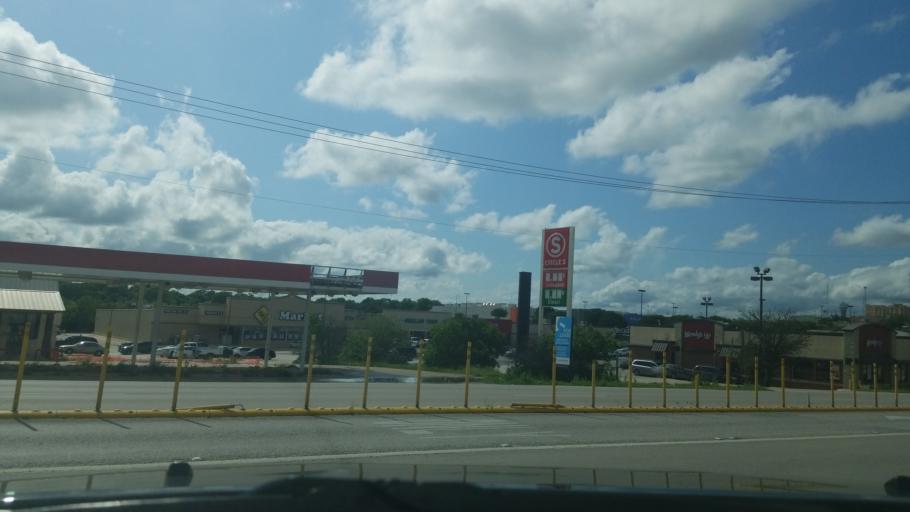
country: US
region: Texas
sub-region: Wise County
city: Decatur
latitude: 33.2256
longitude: -97.5940
